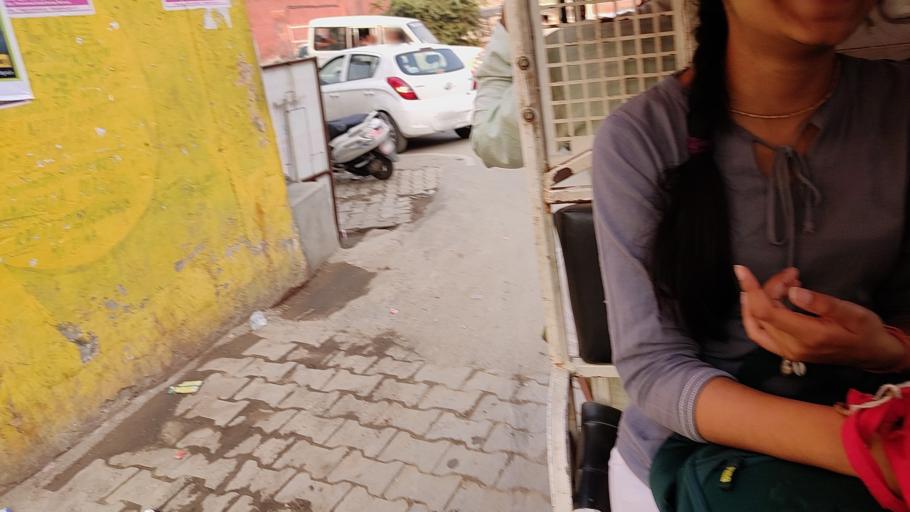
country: IN
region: Uttar Pradesh
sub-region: Mathura
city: Mathura
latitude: 27.5092
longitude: 77.6710
